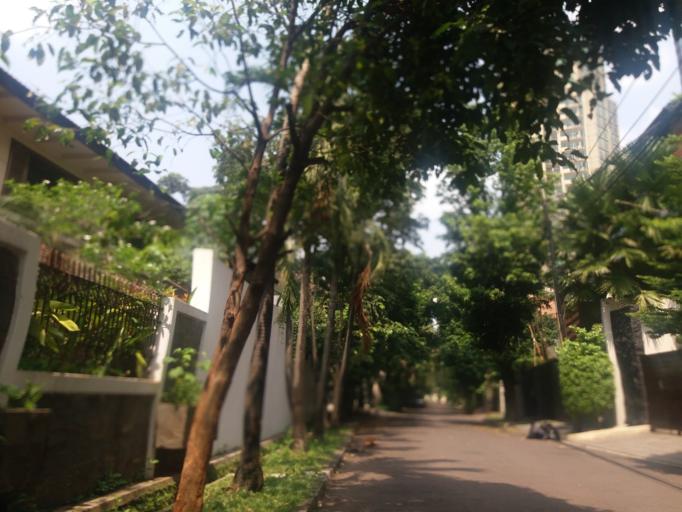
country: ID
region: Jakarta Raya
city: Jakarta
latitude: -6.2264
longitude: 106.8283
